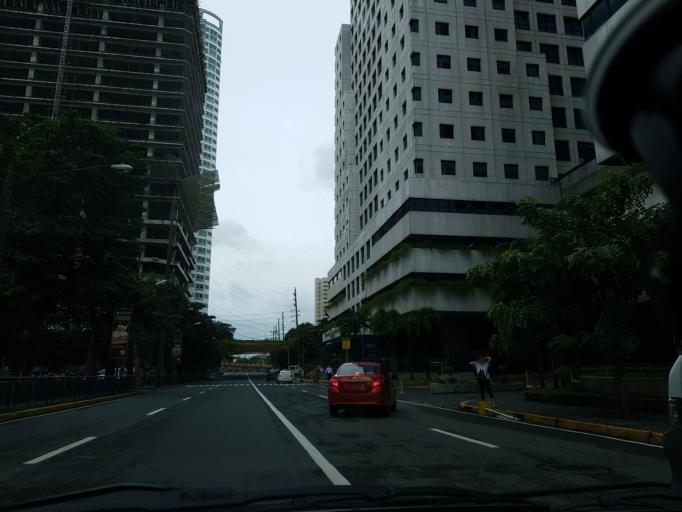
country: PH
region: Metro Manila
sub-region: Pasig
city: Pasig City
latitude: 14.5830
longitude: 121.0615
